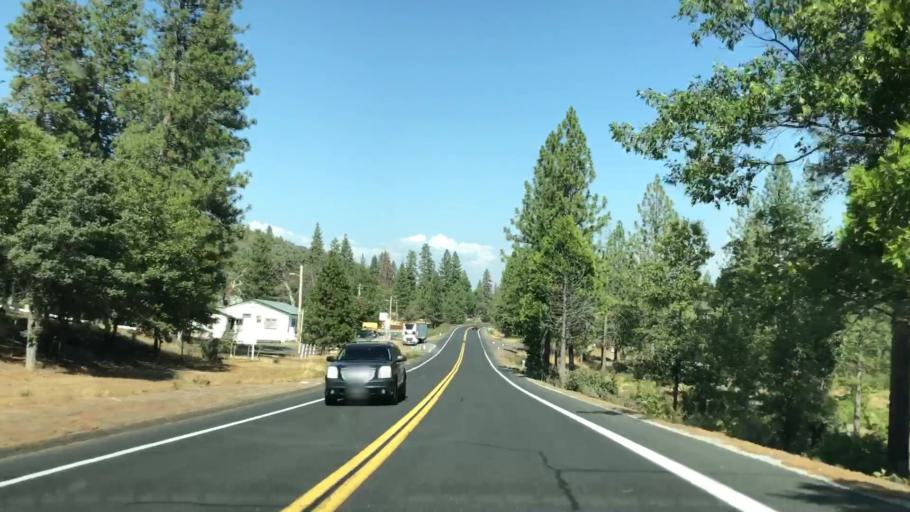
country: US
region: California
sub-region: Tuolumne County
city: Tuolumne City
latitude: 37.8143
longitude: -120.0643
